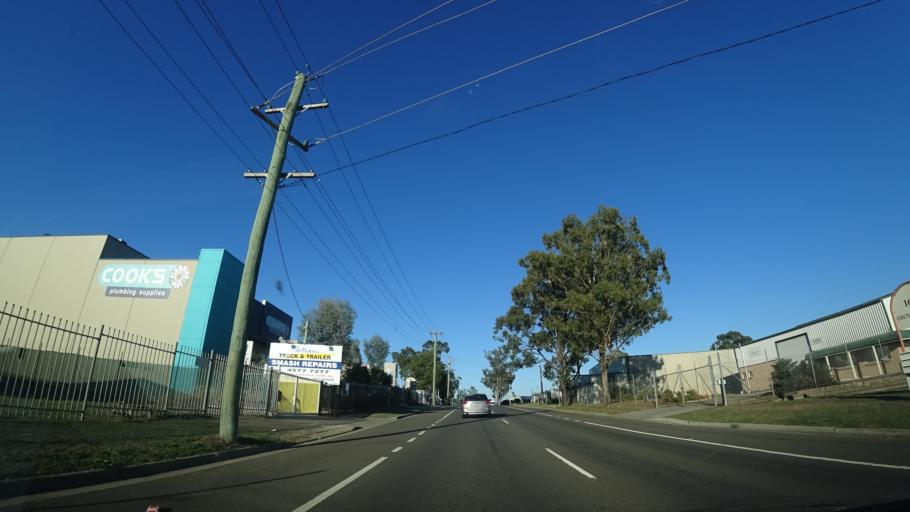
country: AU
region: New South Wales
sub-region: Hawkesbury
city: South Windsor
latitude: -33.6265
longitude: 150.8371
